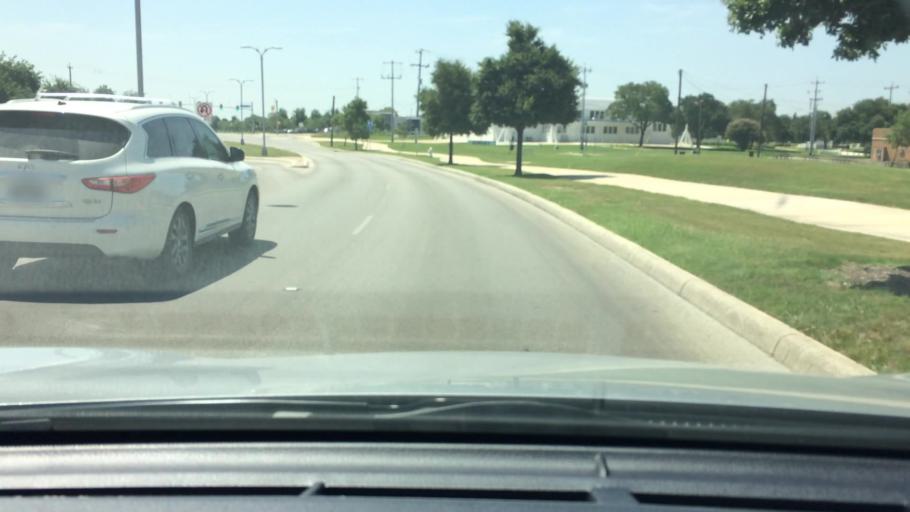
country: US
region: Texas
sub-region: Bexar County
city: San Antonio
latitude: 29.3454
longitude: -98.4449
